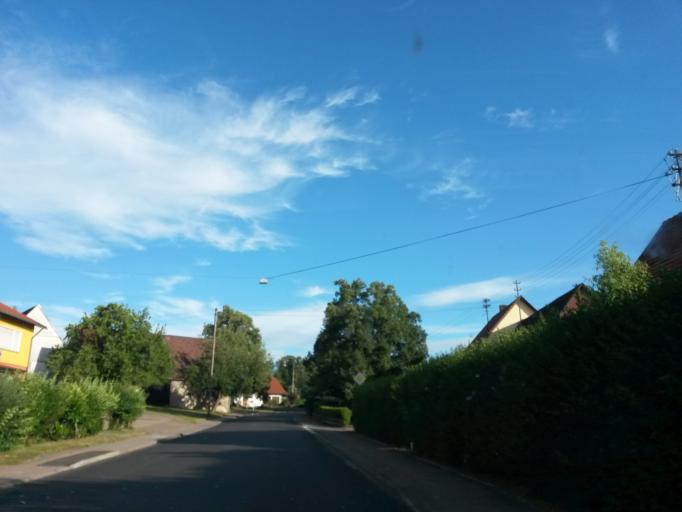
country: DE
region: Baden-Wuerttemberg
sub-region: Regierungsbezirk Stuttgart
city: Ellenberg
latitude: 49.0741
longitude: 10.2075
